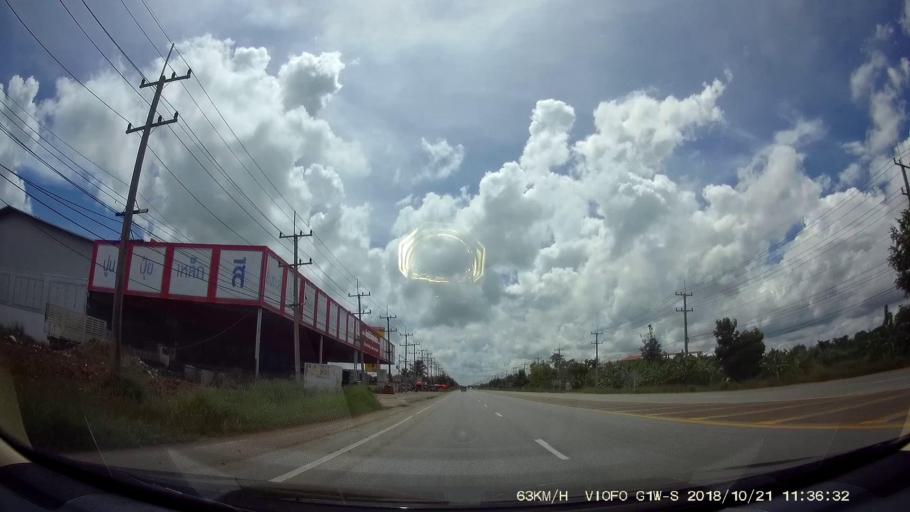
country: TH
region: Chaiyaphum
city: Chaiyaphum
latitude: 15.7185
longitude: 102.0162
